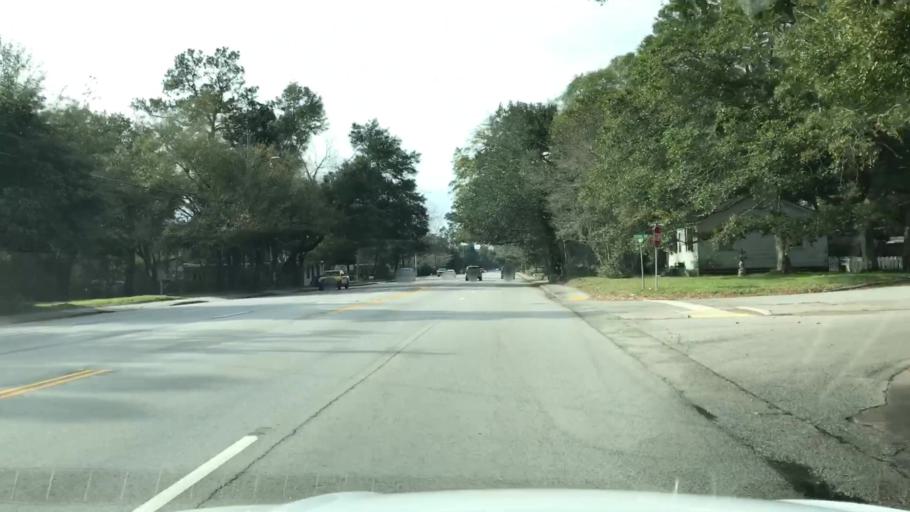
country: US
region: South Carolina
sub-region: Charleston County
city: Charleston
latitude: 32.7604
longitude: -79.9908
